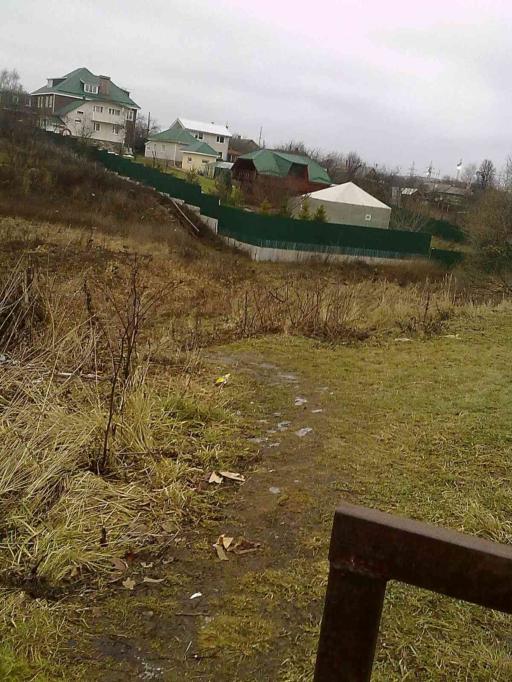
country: RU
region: Moskovskaya
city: Gorki Vtoryye
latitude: 55.6746
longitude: 37.1545
